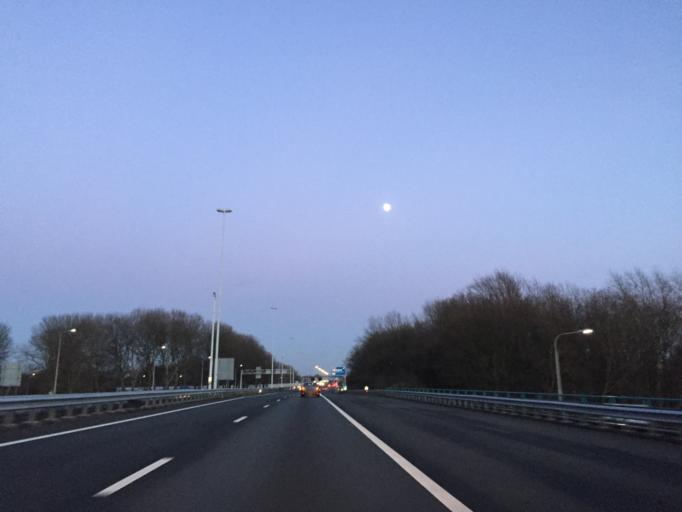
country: NL
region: South Holland
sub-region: Gemeente Rotterdam
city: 's-Gravenland
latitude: 51.9507
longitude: 4.5298
